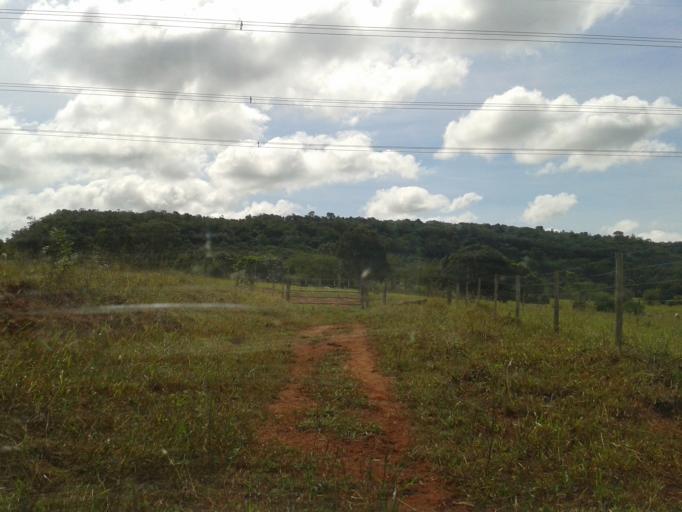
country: BR
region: Minas Gerais
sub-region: Campina Verde
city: Campina Verde
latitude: -19.4257
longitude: -49.6948
